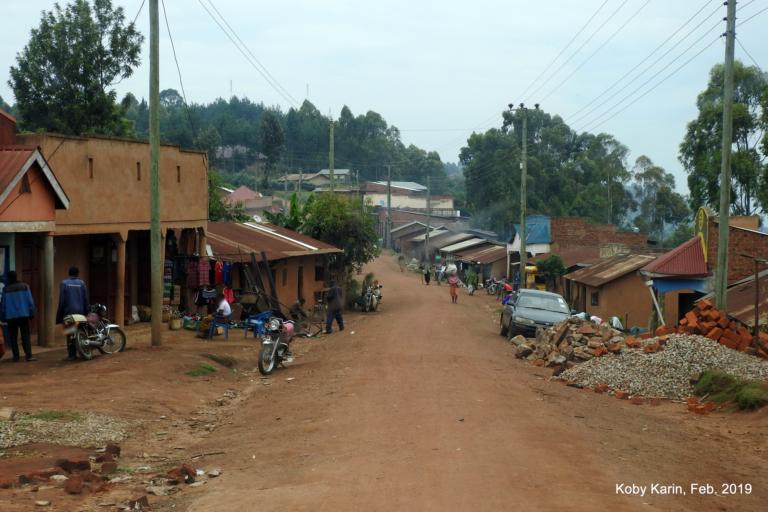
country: UG
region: Western Region
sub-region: Kabale District
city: Kabale
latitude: -1.2387
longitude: 29.9115
